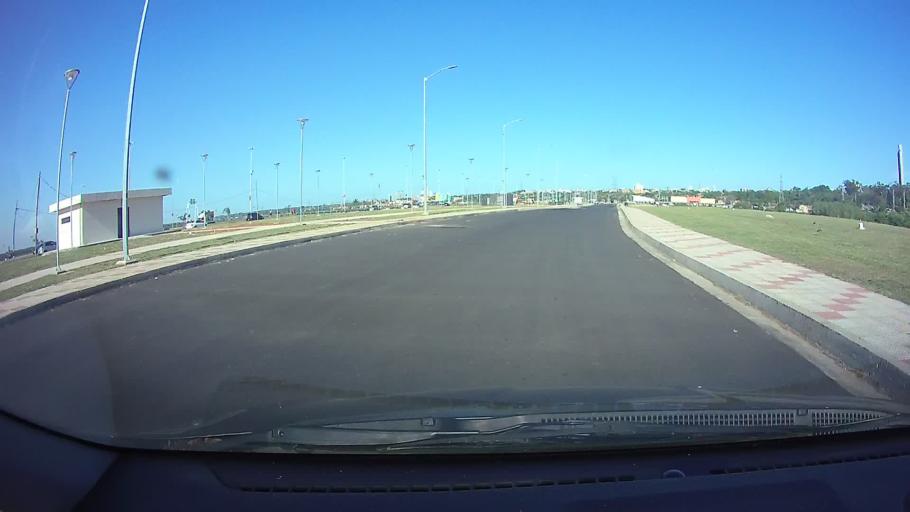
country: PY
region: Asuncion
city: Asuncion
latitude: -25.2766
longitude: -57.6276
